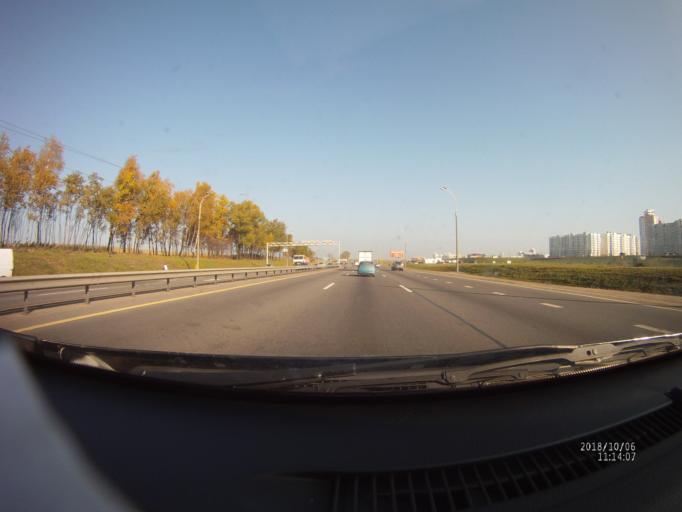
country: BY
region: Minsk
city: Zhdanovichy
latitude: 53.9138
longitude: 27.4112
